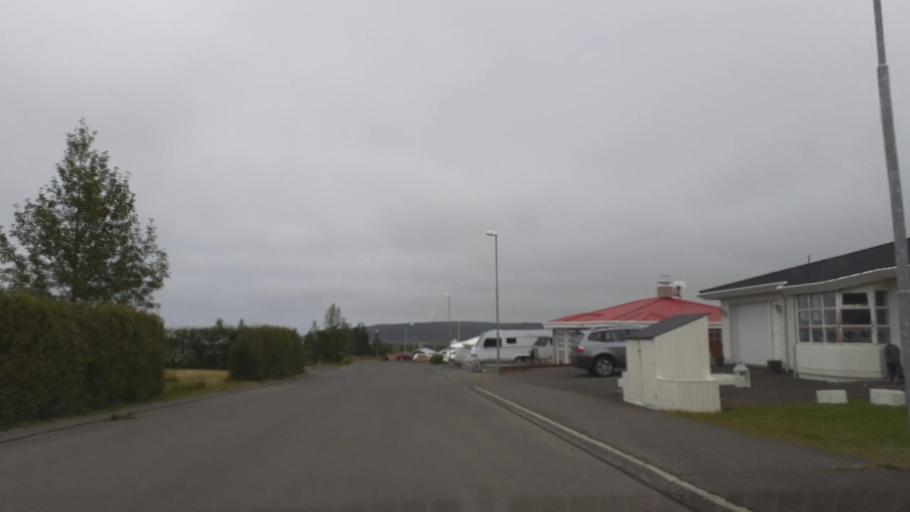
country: IS
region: Northeast
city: Dalvik
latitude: 65.9682
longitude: -18.5446
